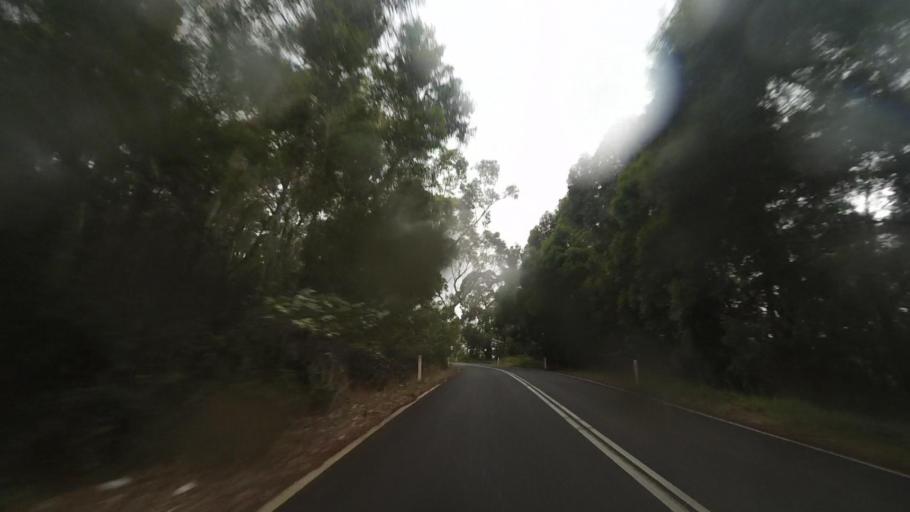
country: AU
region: New South Wales
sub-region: Wollongong
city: Mount Keira
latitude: -34.3981
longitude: 150.8442
